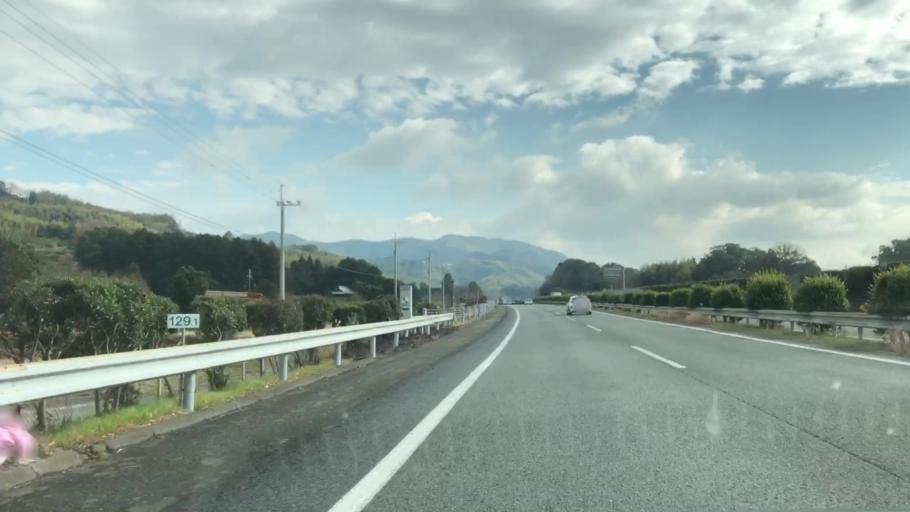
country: JP
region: Fukuoka
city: Setakamachi-takayanagi
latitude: 33.1201
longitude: 130.5223
